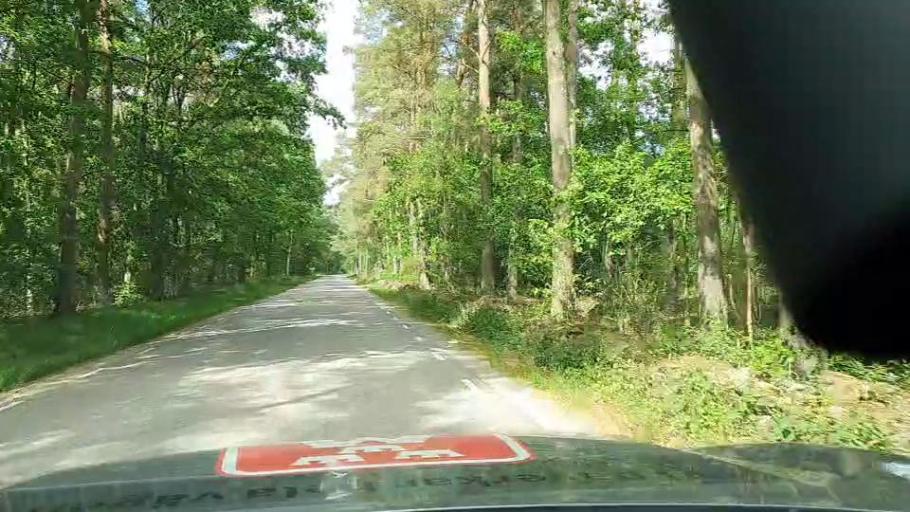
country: SE
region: Blekinge
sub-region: Karlshamns Kommun
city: Morrum
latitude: 56.0998
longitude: 14.6870
